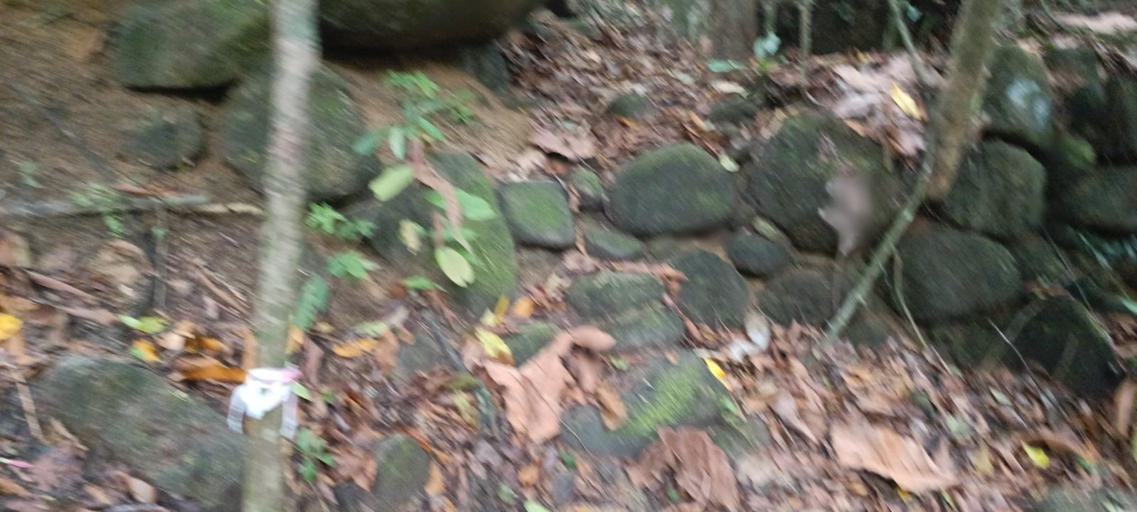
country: MY
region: Penang
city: Bukit Mertajam
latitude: 5.3586
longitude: 100.4890
